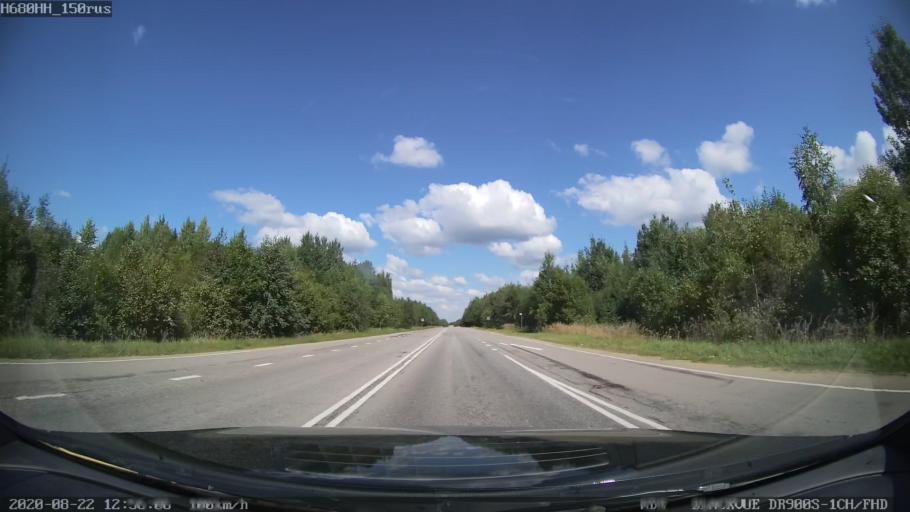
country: RU
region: Tverskaya
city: Rameshki
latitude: 57.5515
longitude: 36.3125
